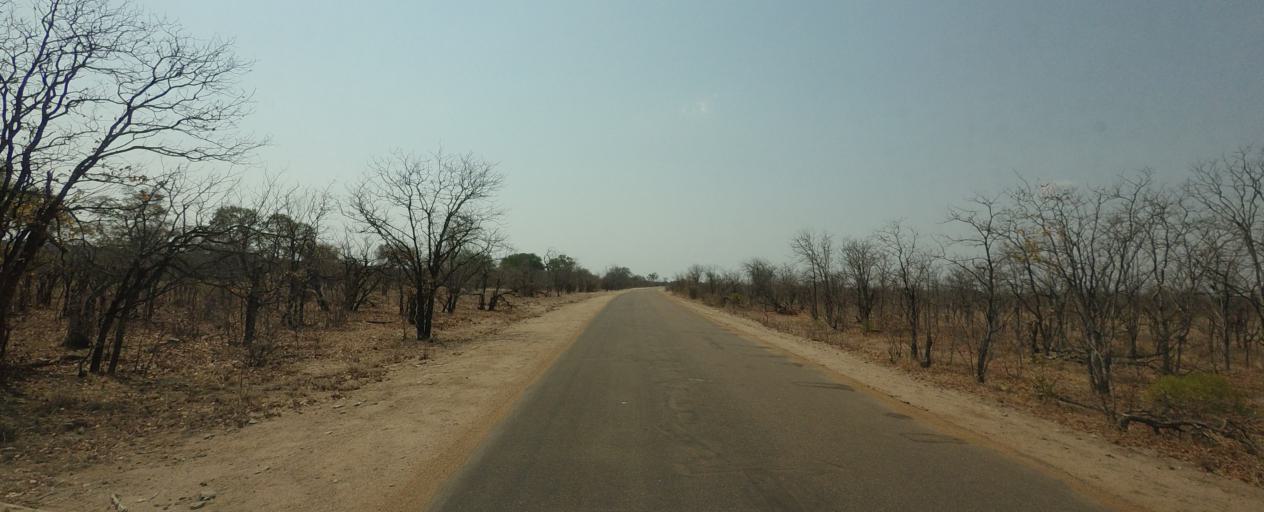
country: ZA
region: Limpopo
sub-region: Mopani District Municipality
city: Phalaborwa
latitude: -23.3709
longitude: 31.3205
